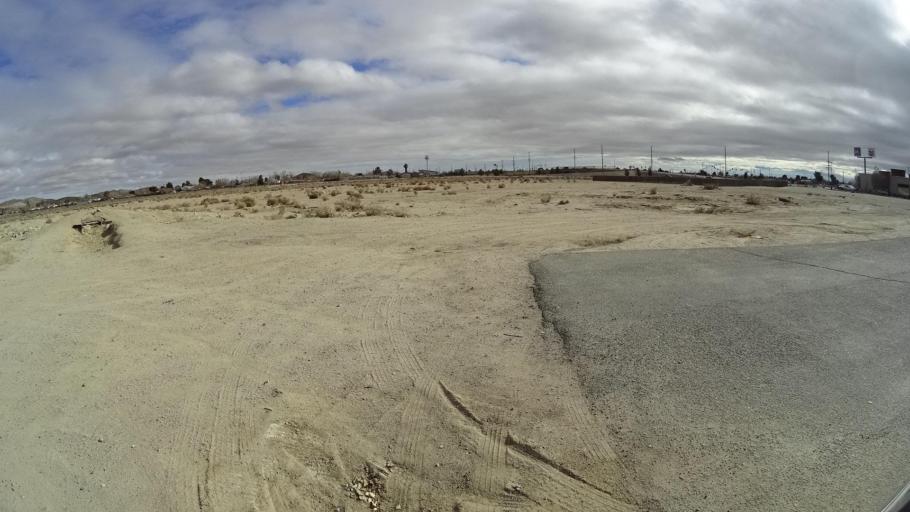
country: US
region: California
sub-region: Kern County
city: Rosamond
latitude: 34.8662
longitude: -118.1759
